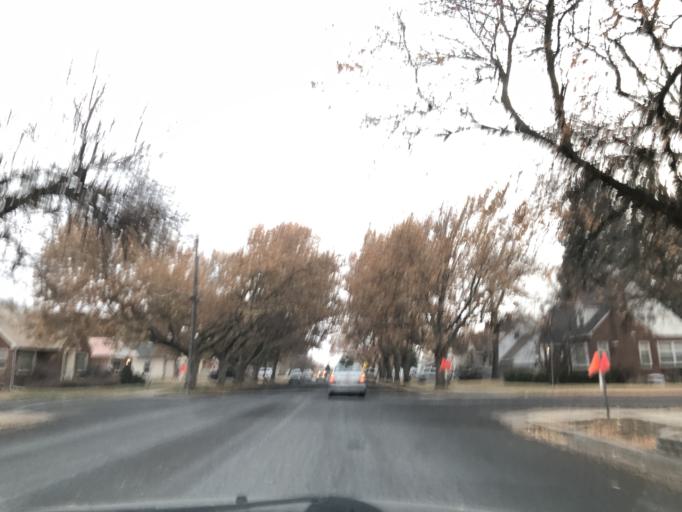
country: US
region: Utah
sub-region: Cache County
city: Logan
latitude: 41.7431
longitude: -111.8295
